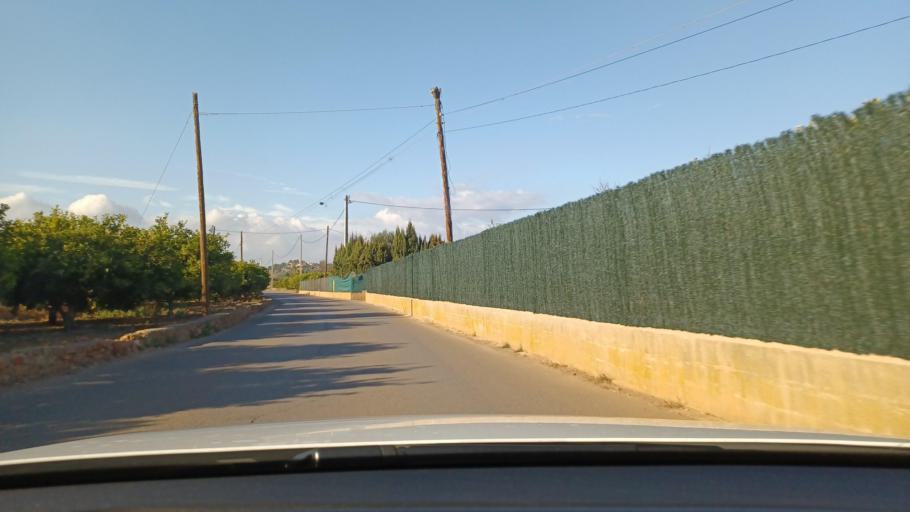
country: ES
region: Valencia
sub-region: Provincia de Castello
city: Betxi
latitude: 39.9480
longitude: -0.2240
